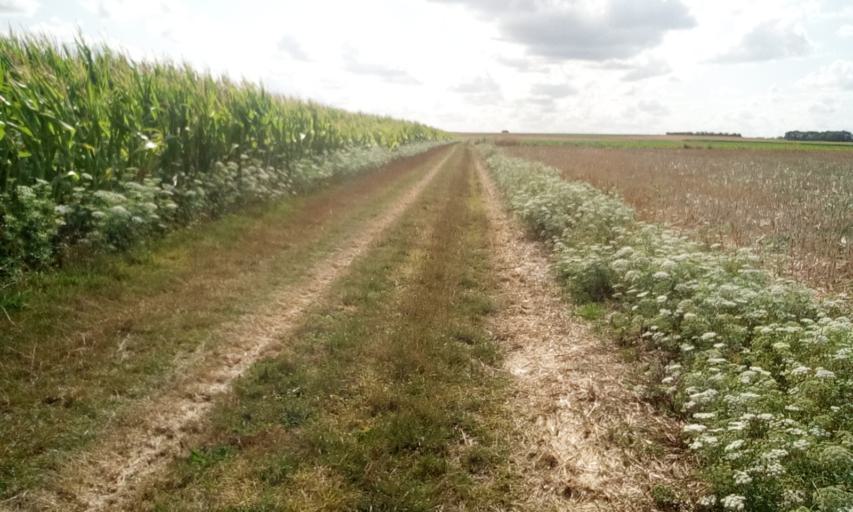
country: FR
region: Lower Normandy
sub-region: Departement du Calvados
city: Saint-Sylvain
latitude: 49.0728
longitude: -0.2333
